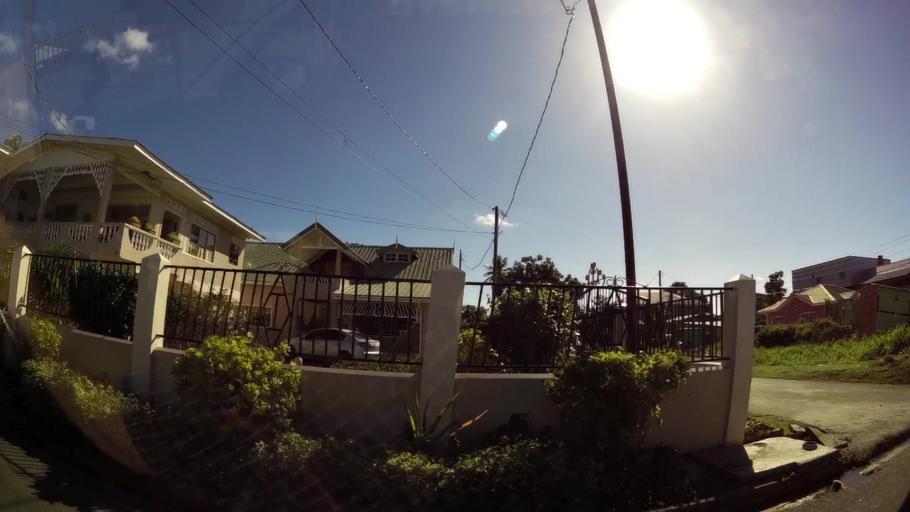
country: TT
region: Tobago
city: Scarborough
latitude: 11.1586
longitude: -60.8171
